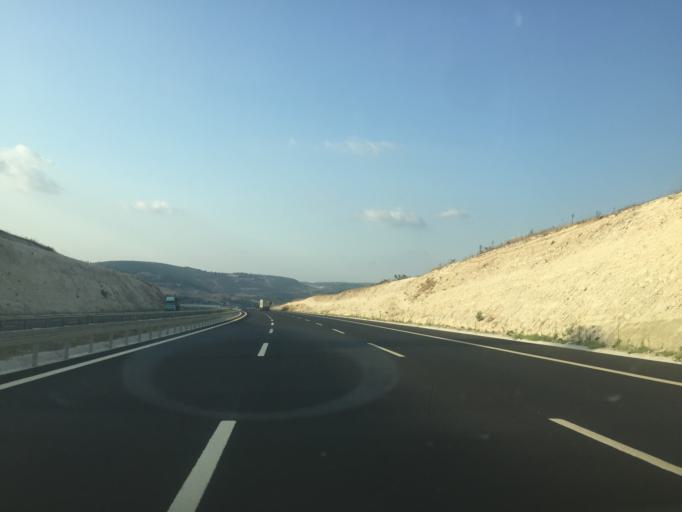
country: TR
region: Balikesir
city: Ertugrul
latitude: 39.5664
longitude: 27.7027
